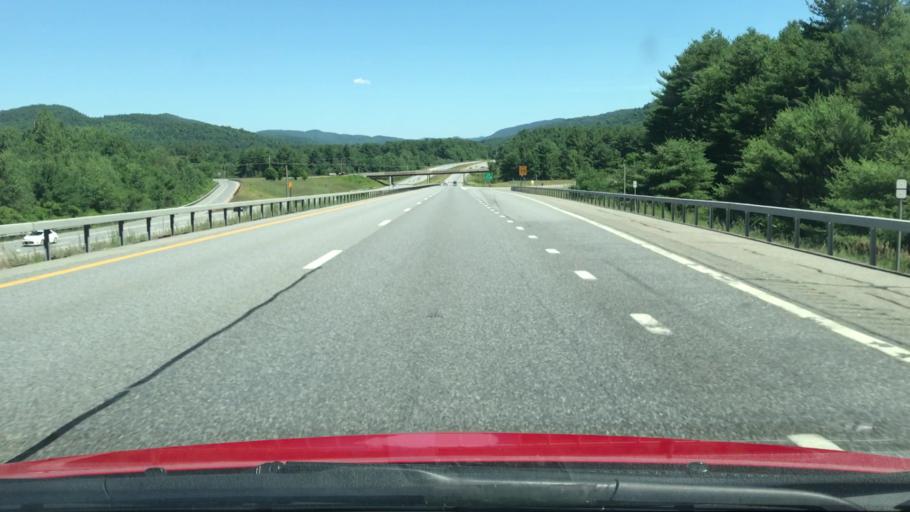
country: US
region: New York
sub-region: Warren County
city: Warrensburg
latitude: 43.4827
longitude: -73.7543
